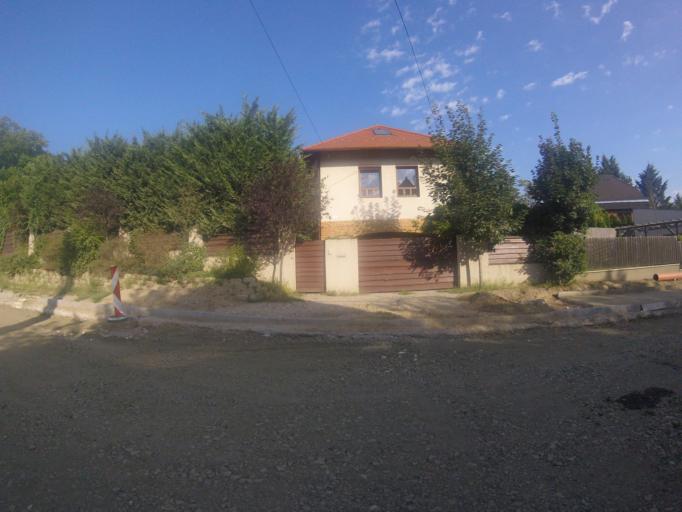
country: HU
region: Pest
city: Veresegyhaz
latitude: 47.6509
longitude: 19.2764
